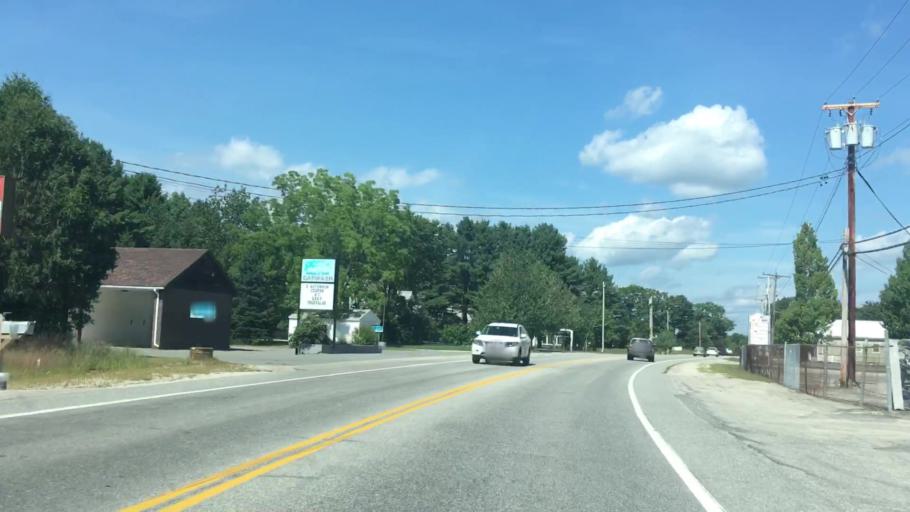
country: US
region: Maine
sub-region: Cumberland County
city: New Gloucester
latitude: 43.8948
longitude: -70.3281
